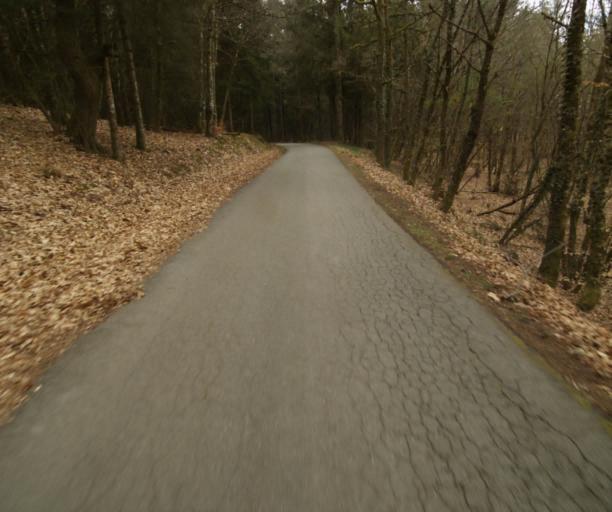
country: FR
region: Limousin
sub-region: Departement de la Correze
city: Correze
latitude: 45.3221
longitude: 1.9429
